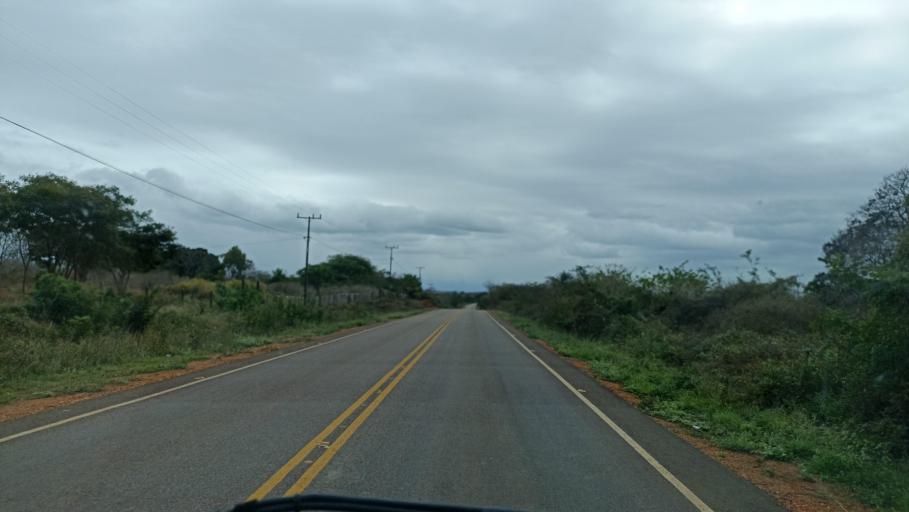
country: BR
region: Bahia
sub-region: Andarai
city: Vera Cruz
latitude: -12.9835
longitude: -41.0110
